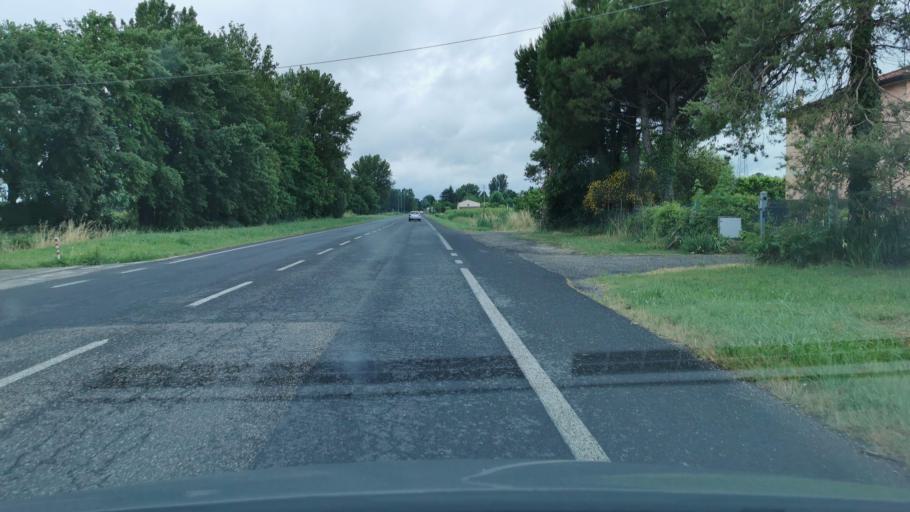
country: IT
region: Emilia-Romagna
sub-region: Provincia di Ravenna
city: Cotignola
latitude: 44.3751
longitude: 11.9462
